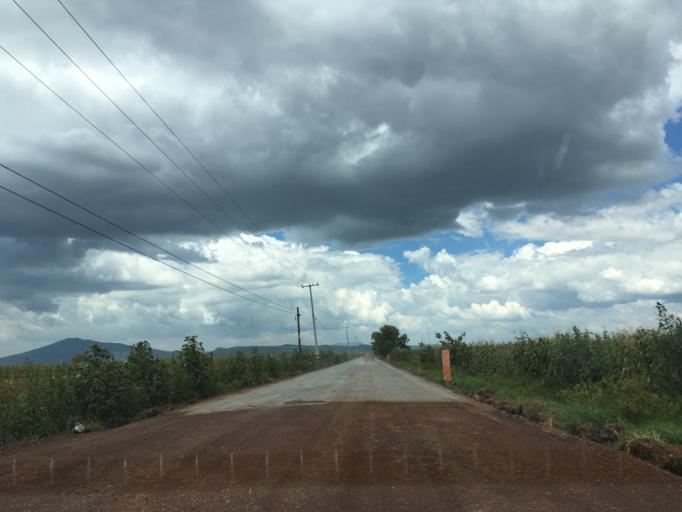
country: MX
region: Michoacan
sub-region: Zacapu
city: Naranja de Tapia
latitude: 19.8281
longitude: -101.7119
